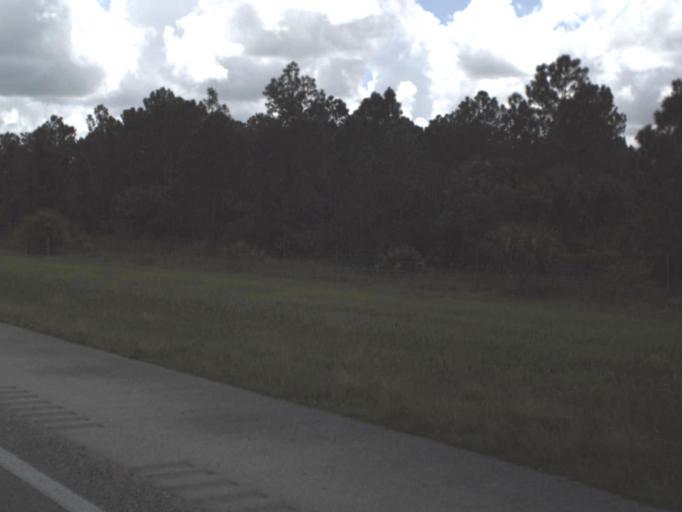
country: US
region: Florida
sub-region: Collier County
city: Golden Gate
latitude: 26.1529
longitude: -81.5579
